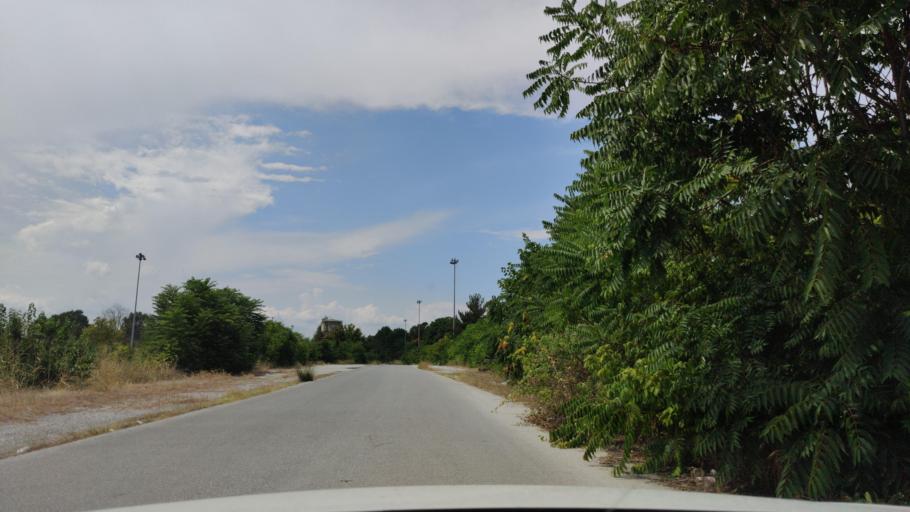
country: GR
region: Central Macedonia
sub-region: Nomos Serron
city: Serres
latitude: 41.0739
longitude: 23.5399
